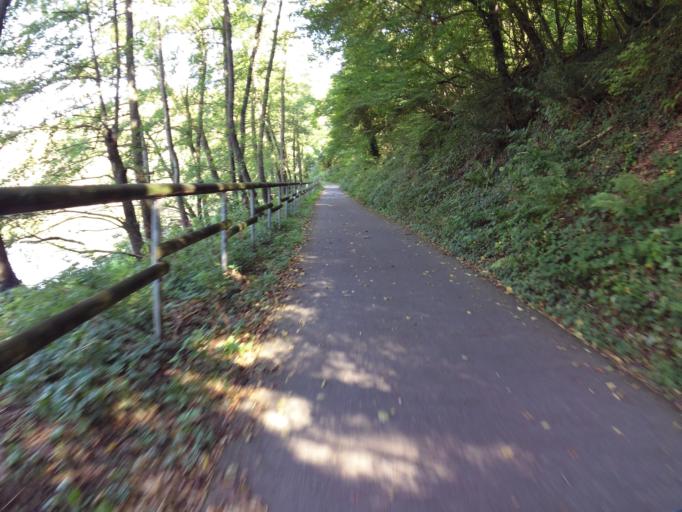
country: LU
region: Grevenmacher
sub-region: Canton d'Echternach
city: Rosport
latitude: 49.7809
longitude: 6.5165
